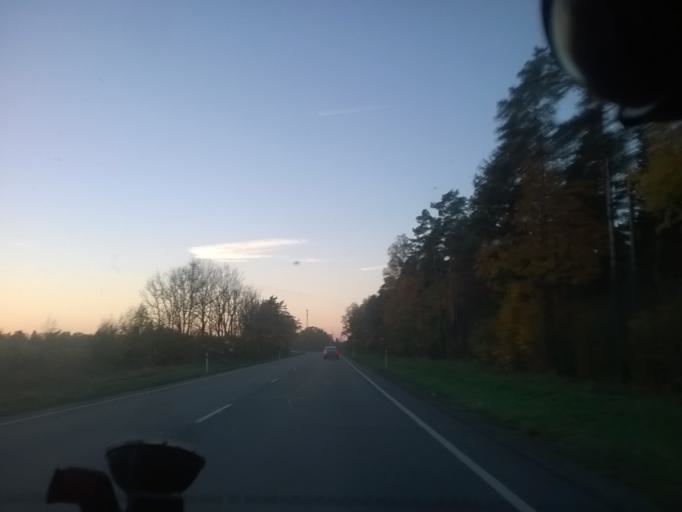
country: EE
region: Laeaene
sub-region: Ridala Parish
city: Uuemoisa
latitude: 58.9585
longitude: 23.7175
